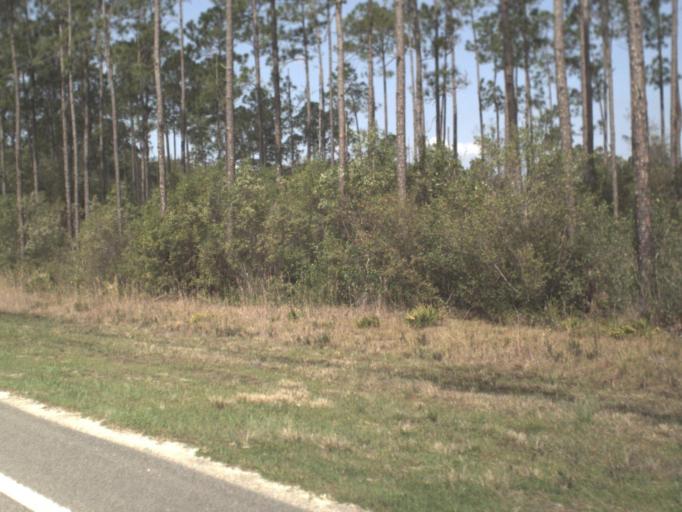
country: US
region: Florida
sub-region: Gadsden County
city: Gretna
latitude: 30.3836
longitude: -84.7284
